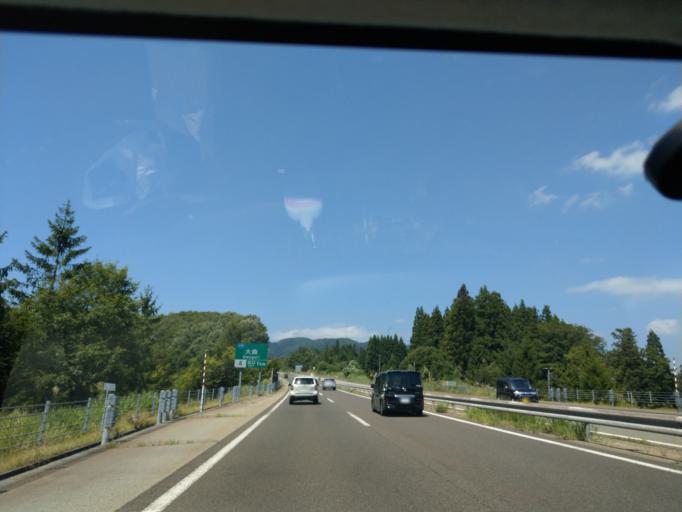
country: JP
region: Akita
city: Omagari
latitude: 39.4190
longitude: 140.4353
